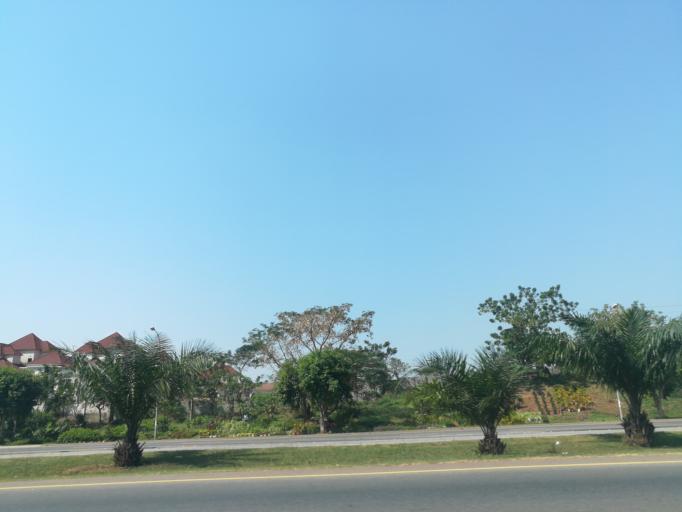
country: NG
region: Abuja Federal Capital Territory
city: Abuja
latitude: 9.0594
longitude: 7.4537
